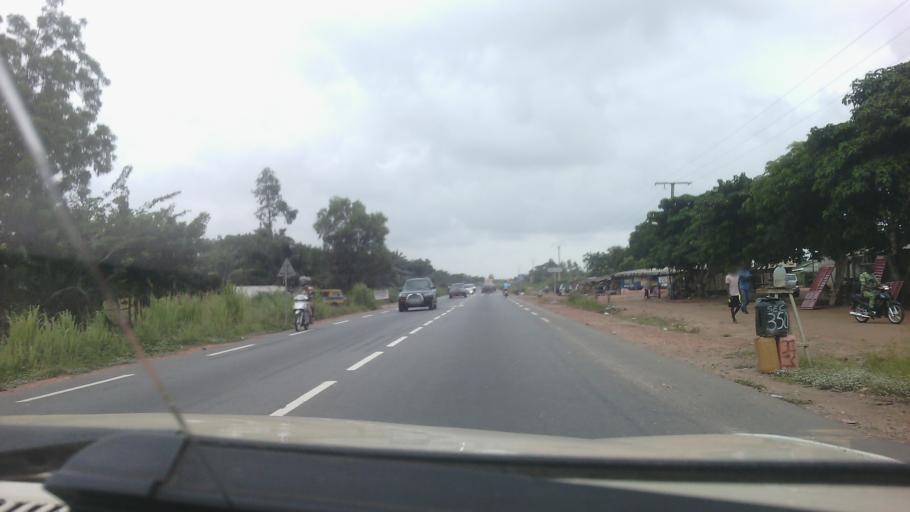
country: BJ
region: Atlantique
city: Ouidah
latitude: 6.3862
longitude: 2.0088
